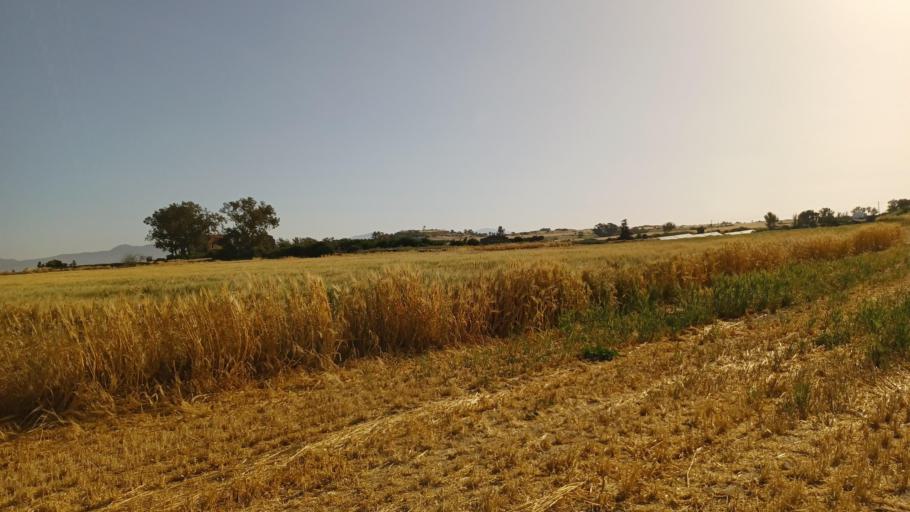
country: CY
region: Lefkosia
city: Mammari
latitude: 35.1662
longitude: 33.2451
